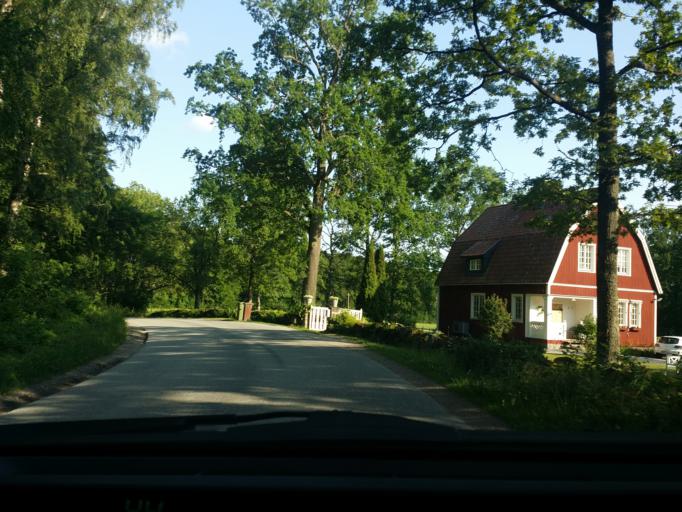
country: SE
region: Vaestmanland
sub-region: Vasteras
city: Vasteras
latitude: 59.5607
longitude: 16.6597
